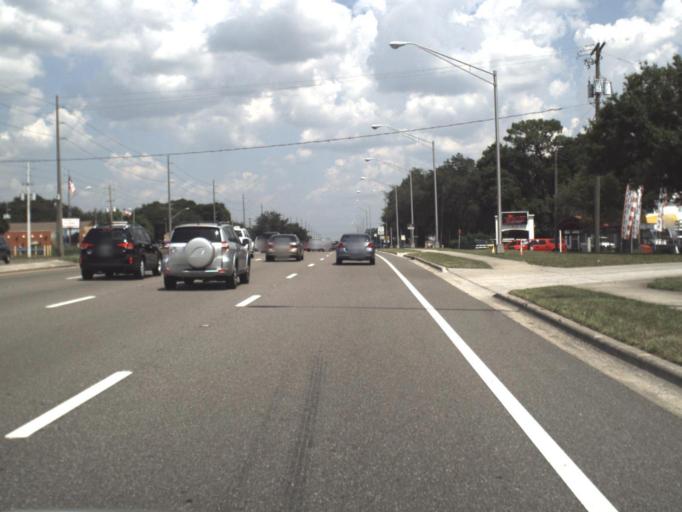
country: US
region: Florida
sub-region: Hillsborough County
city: Brandon
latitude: 27.9376
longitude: -82.2730
